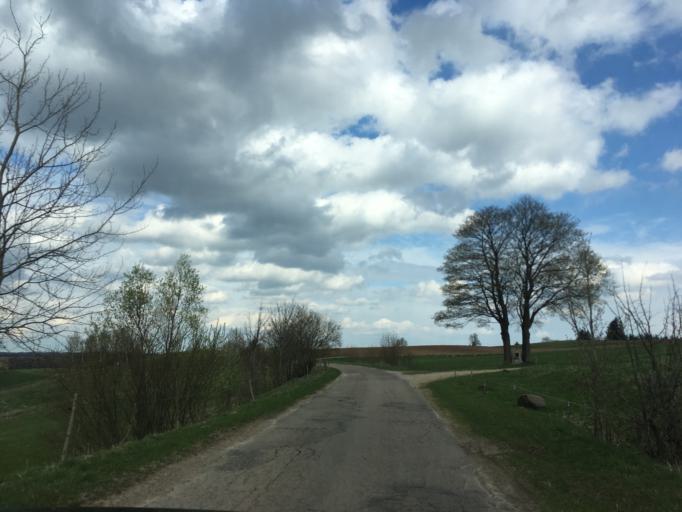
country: PL
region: Podlasie
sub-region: Suwalki
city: Suwalki
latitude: 54.3703
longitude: 22.8941
